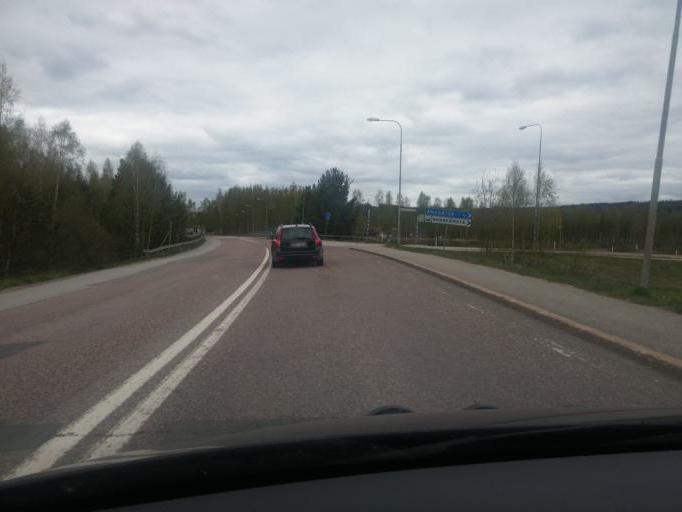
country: SE
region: Gaevleborg
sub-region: Ljusdals Kommun
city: Ljusdal
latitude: 61.8328
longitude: 16.0688
